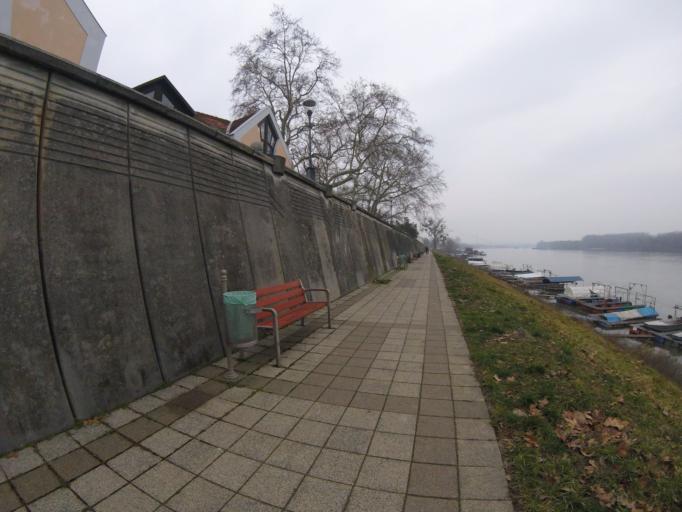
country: HU
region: Baranya
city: Mohacs
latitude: 45.9967
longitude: 18.6908
